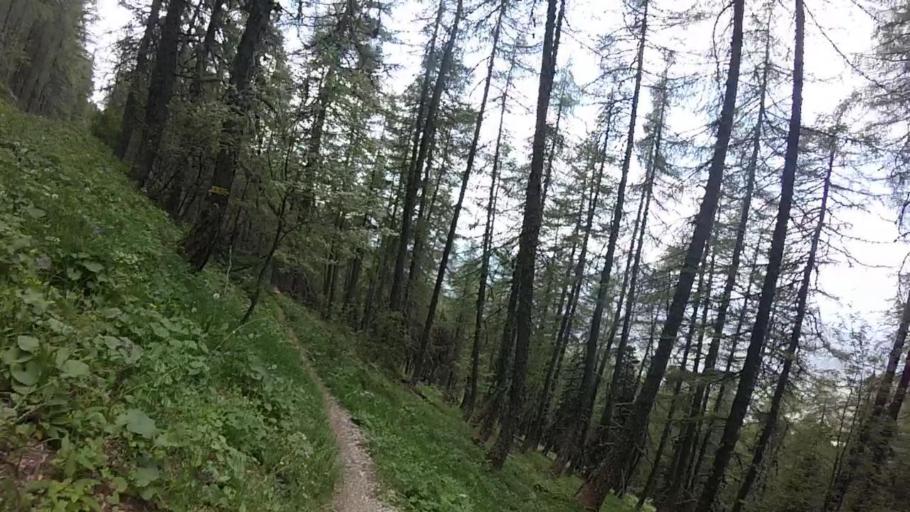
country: FR
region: Provence-Alpes-Cote d'Azur
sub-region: Departement des Alpes-de-Haute-Provence
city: Seyne-les-Alpes
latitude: 44.4121
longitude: 6.3736
